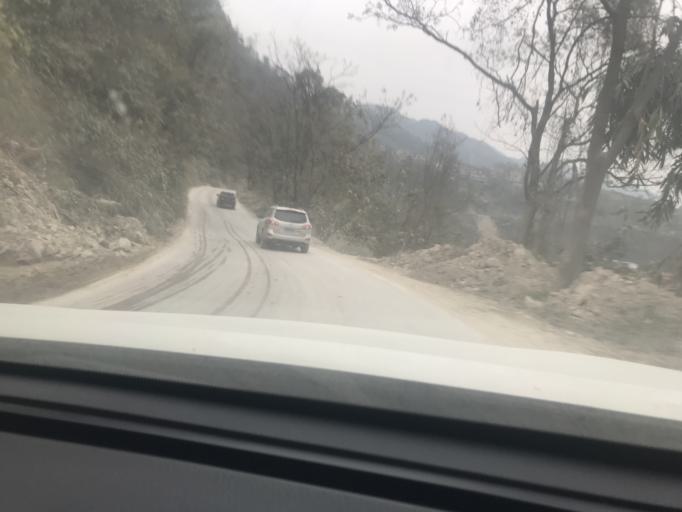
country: CN
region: Guangxi Zhuangzu Zizhiqu
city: Xinzhou
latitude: 24.9914
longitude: 105.8237
